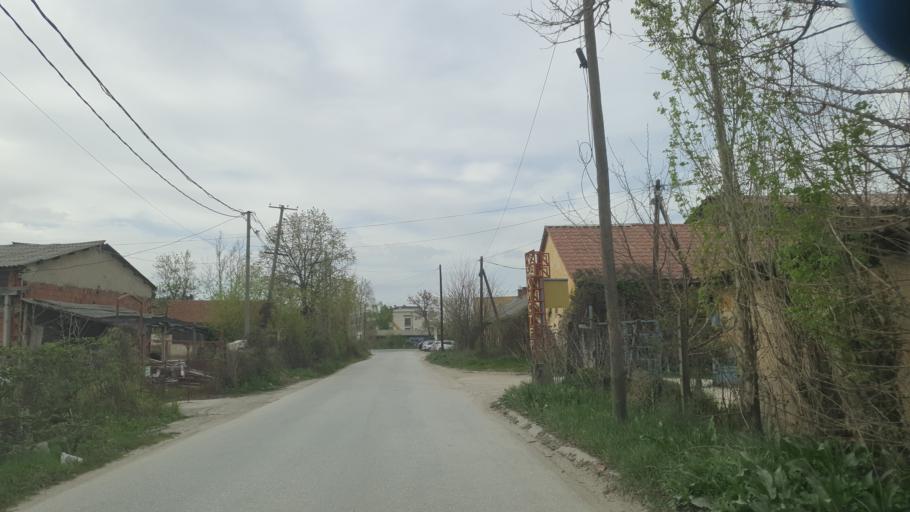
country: MK
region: Bitola
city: Gorno Orizari
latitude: 41.0380
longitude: 21.3498
